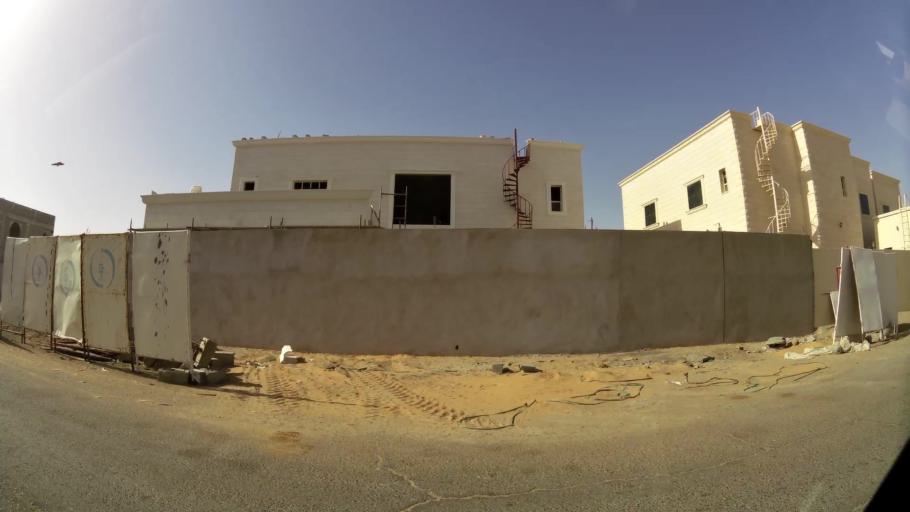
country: OM
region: Al Buraimi
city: Al Buraymi
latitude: 24.3583
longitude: 55.7953
